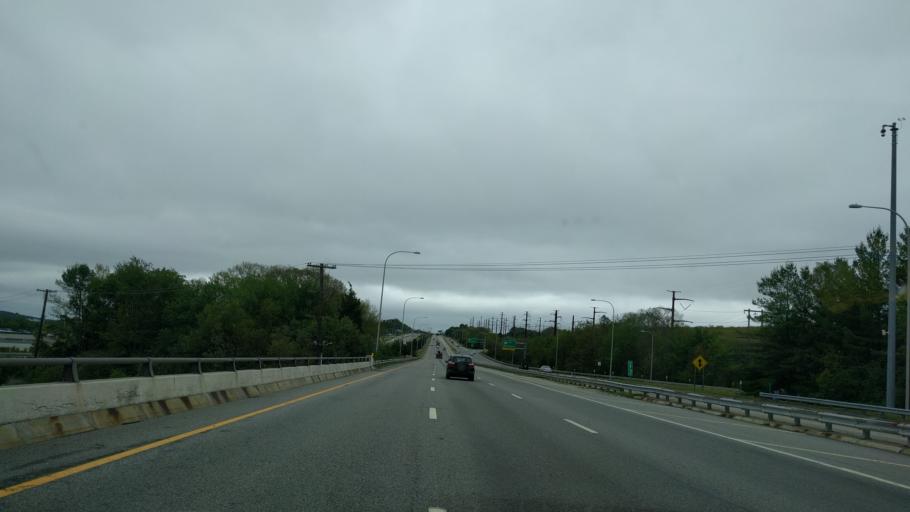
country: US
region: Rhode Island
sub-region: Providence County
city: Johnston
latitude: 41.8290
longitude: -71.5173
